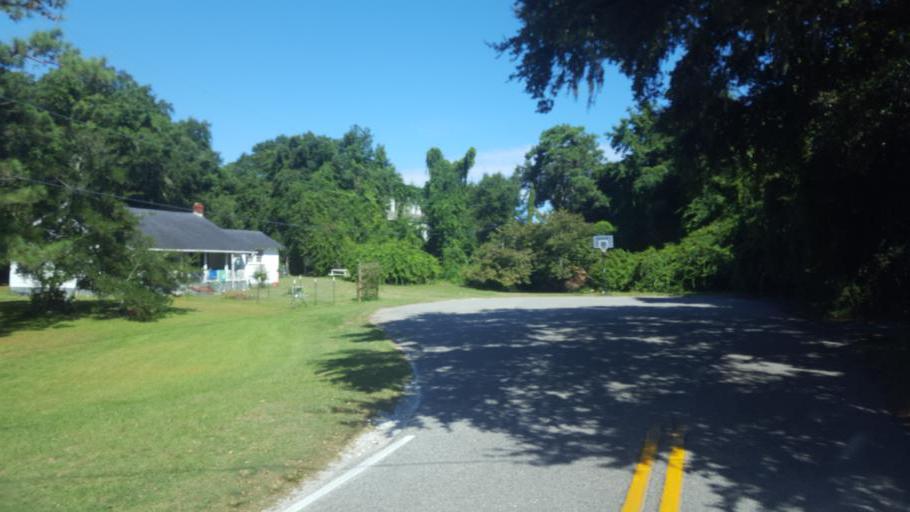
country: US
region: North Carolina
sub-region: Dare County
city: Kill Devil Hills
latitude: 36.0208
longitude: -75.7124
